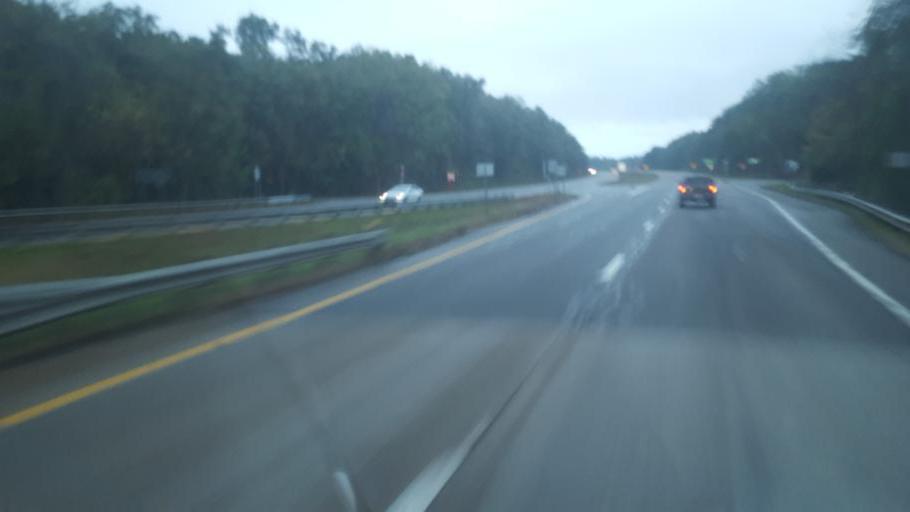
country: US
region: Ohio
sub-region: Ashland County
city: Ashland
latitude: 40.7807
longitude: -82.3780
